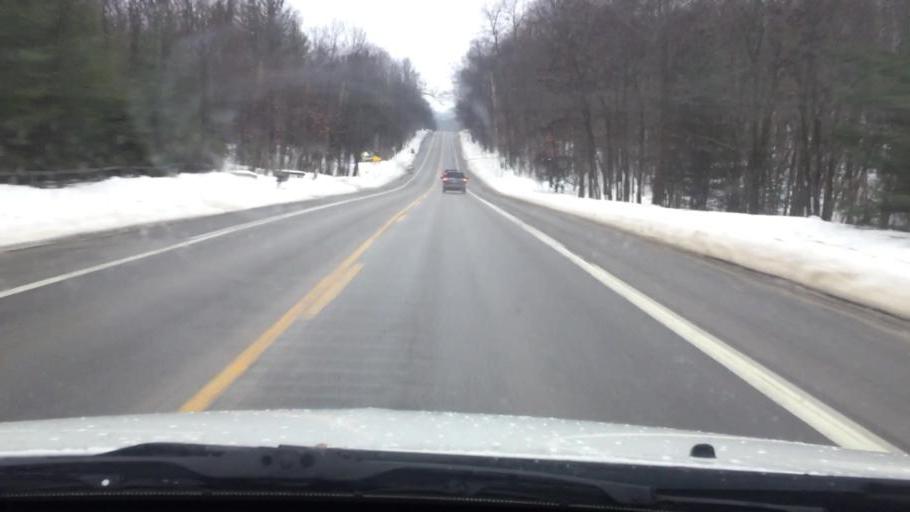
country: US
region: Michigan
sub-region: Charlevoix County
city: East Jordan
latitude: 45.2427
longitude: -85.1811
